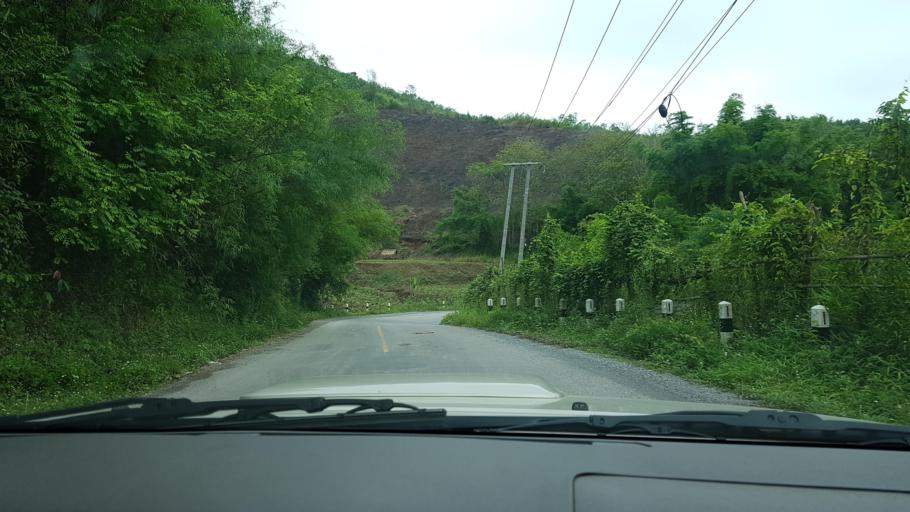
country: LA
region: Oudomxai
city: Muang Xay
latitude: 20.7343
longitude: 102.0238
